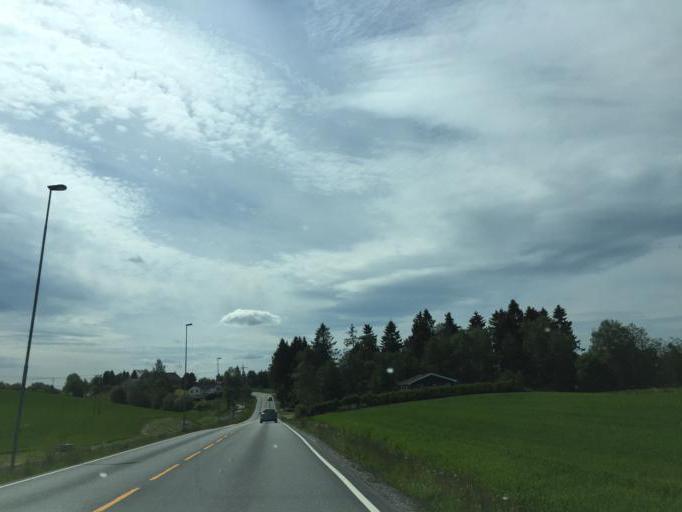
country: NO
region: Akershus
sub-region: Nes
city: Arnes
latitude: 60.1177
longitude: 11.4655
